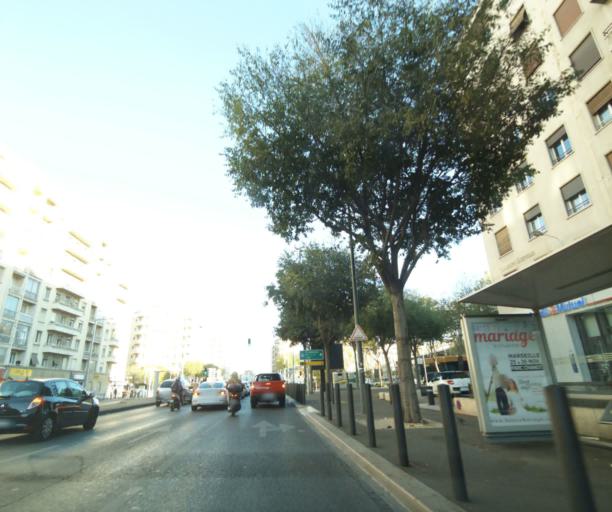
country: FR
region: Provence-Alpes-Cote d'Azur
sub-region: Departement des Bouches-du-Rhone
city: Marseille 04
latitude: 43.2991
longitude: 5.4010
